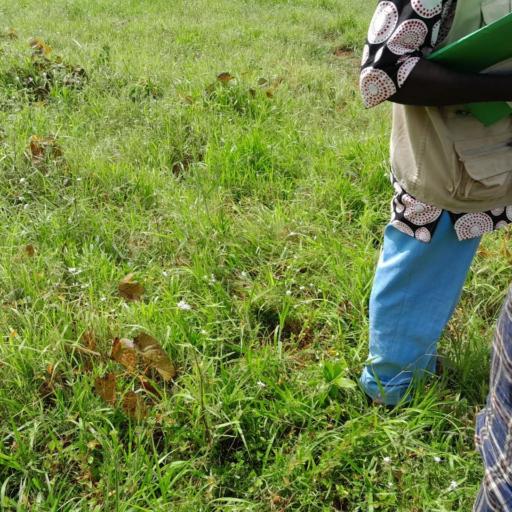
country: GN
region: Boke
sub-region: Boke Prefecture
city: Boke
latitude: 11.0701
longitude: -14.4443
